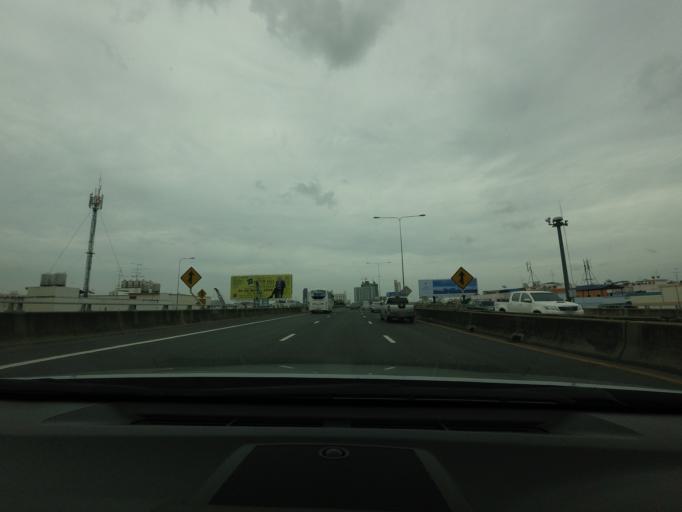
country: TH
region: Bangkok
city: Sathon
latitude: 13.7120
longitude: 100.5199
